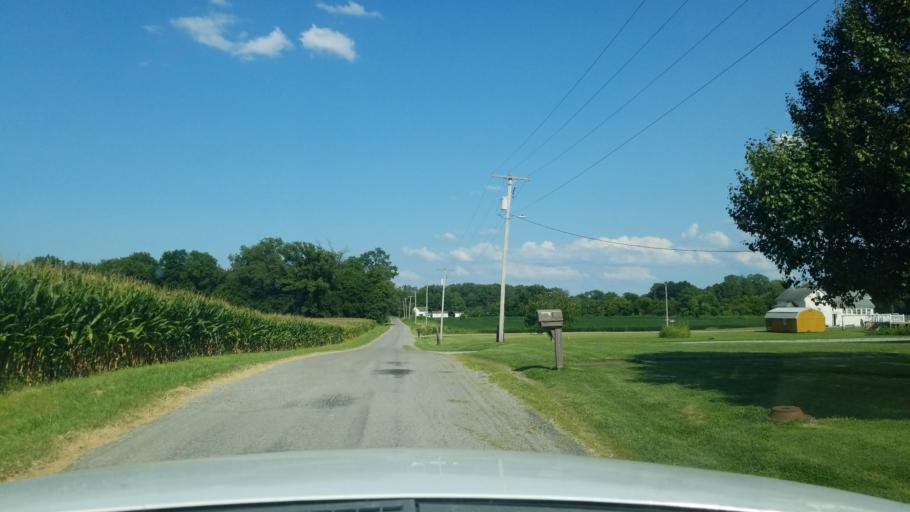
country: US
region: Illinois
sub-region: Saline County
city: Eldorado
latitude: 37.7864
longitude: -88.4946
